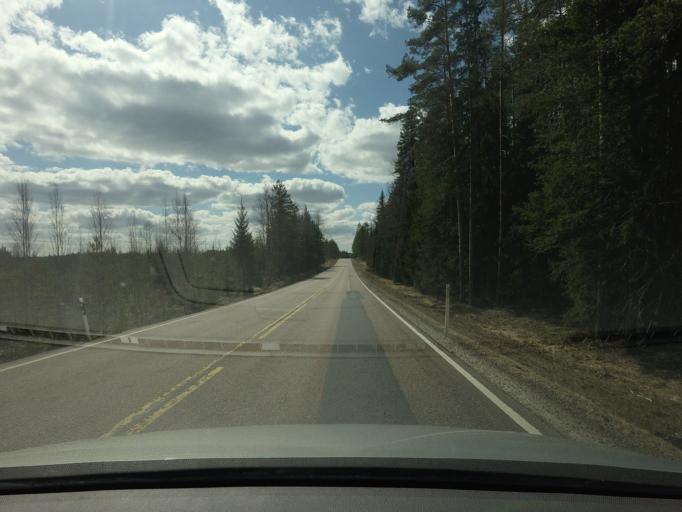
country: FI
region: Kymenlaakso
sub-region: Kotka-Hamina
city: Hamina
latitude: 60.7246
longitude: 27.3200
